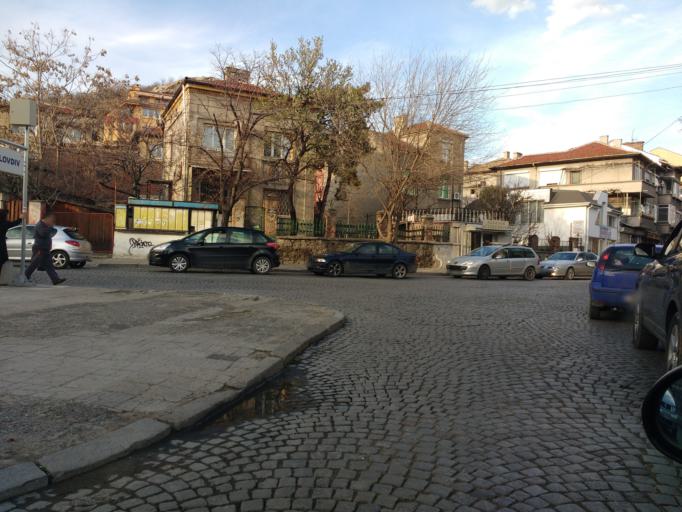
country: BG
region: Plovdiv
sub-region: Obshtina Plovdiv
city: Plovdiv
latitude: 42.1407
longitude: 24.7370
